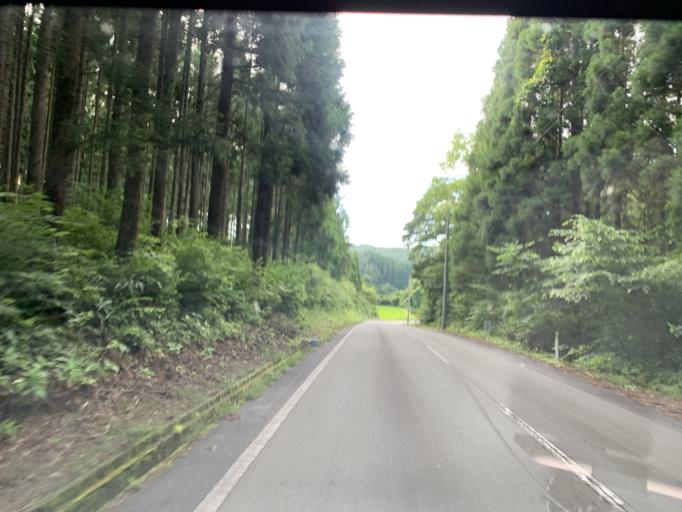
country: JP
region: Iwate
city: Ichinoseki
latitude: 38.8944
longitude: 140.9807
